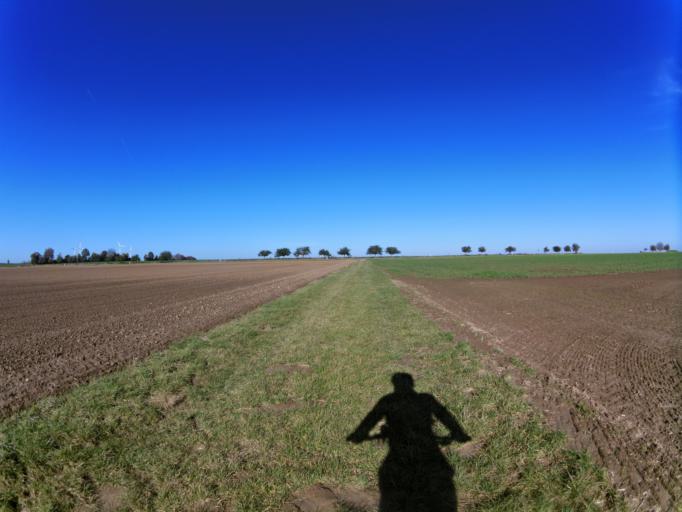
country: DE
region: Bavaria
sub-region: Regierungsbezirk Unterfranken
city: Geroldshausen
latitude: 49.6874
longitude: 9.9171
